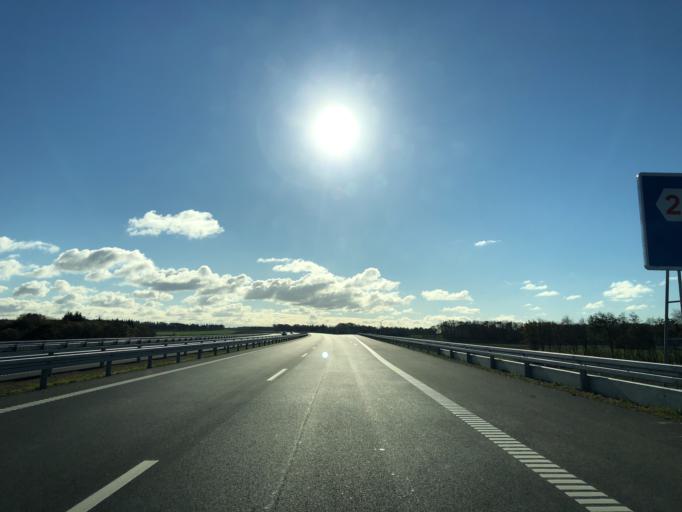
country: DK
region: Central Jutland
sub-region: Herning Kommune
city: Avlum
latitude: 56.2997
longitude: 8.7266
